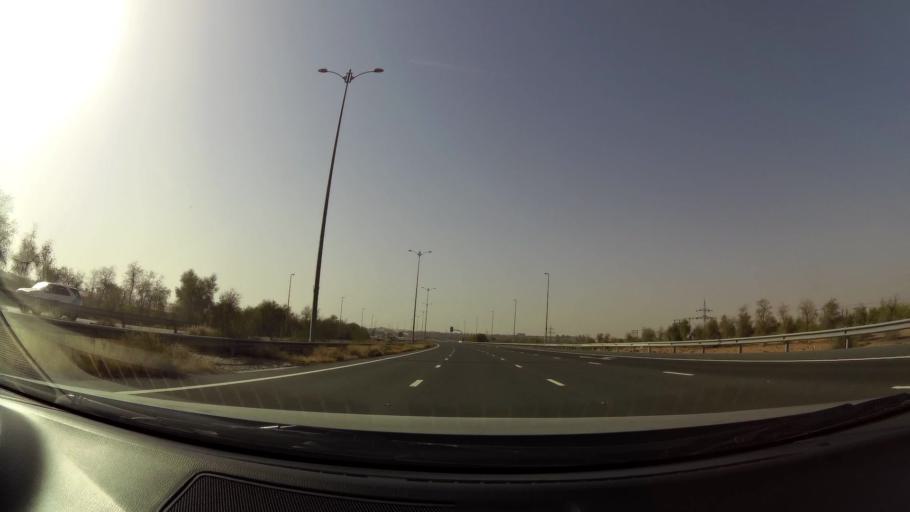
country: OM
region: Al Buraimi
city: Al Buraymi
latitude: 24.6458
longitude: 55.7056
